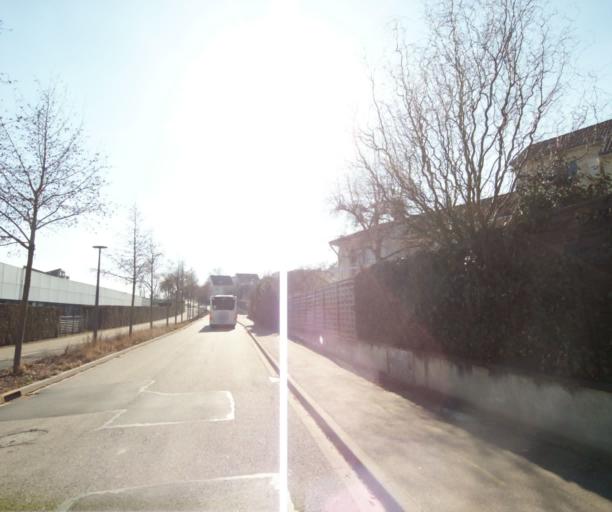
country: FR
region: Lorraine
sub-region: Departement de Meurthe-et-Moselle
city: Vandoeuvre-les-Nancy
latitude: 48.6539
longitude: 6.1761
